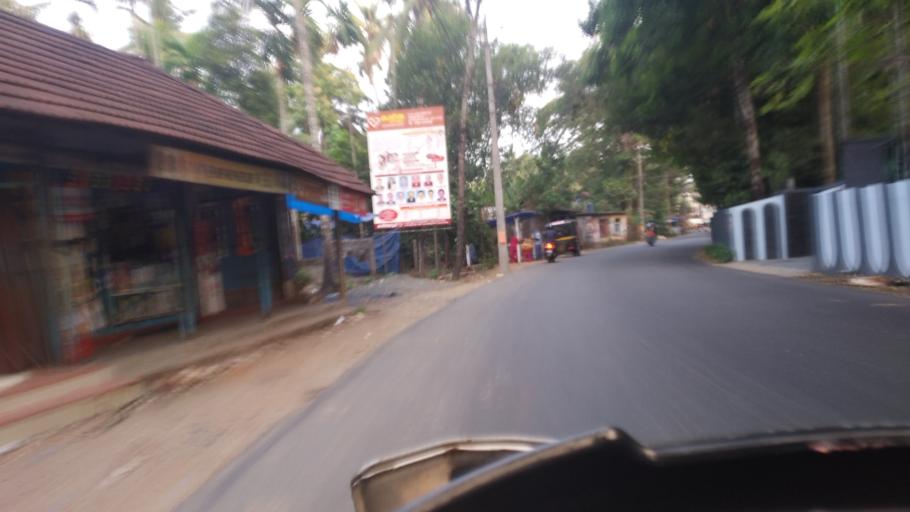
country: IN
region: Kerala
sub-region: Thrissur District
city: Kodungallur
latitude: 10.1857
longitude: 76.2040
